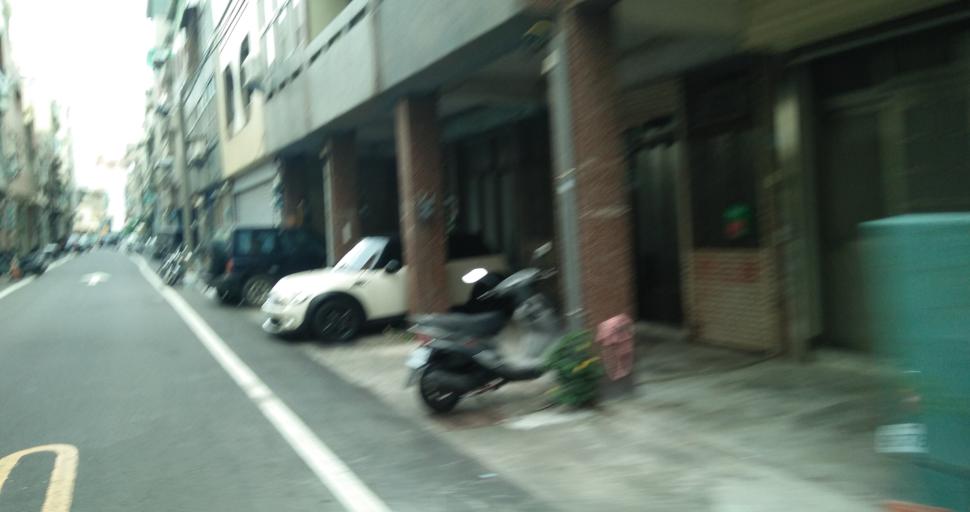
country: TW
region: Taiwan
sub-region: Hsinchu
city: Hsinchu
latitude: 24.8051
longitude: 120.9622
